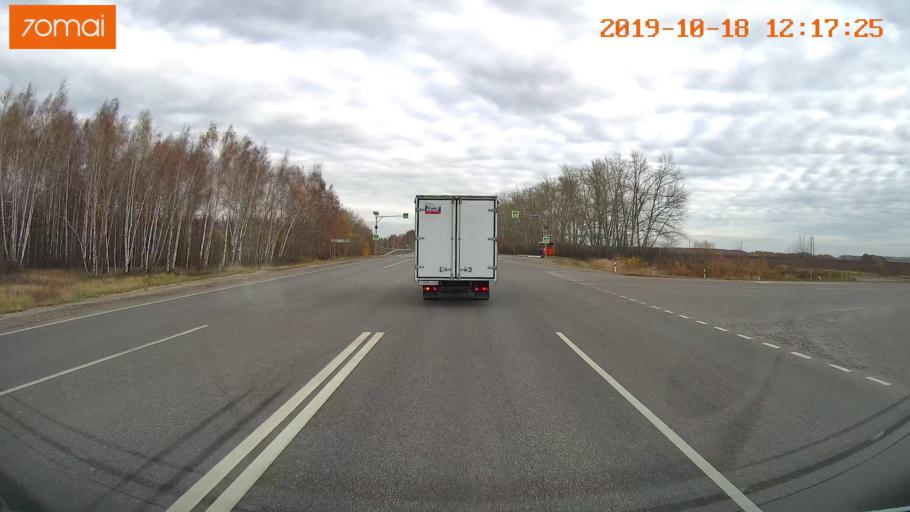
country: RU
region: Rjazan
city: Zakharovo
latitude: 54.4574
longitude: 39.4437
